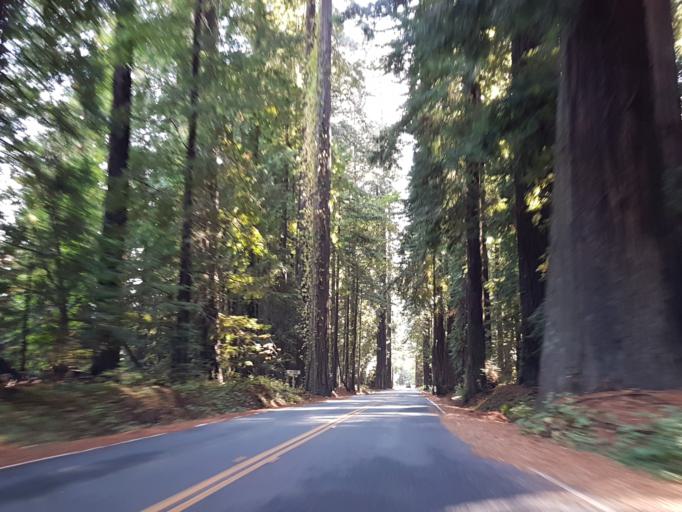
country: US
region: California
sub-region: Humboldt County
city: Rio Dell
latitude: 40.4360
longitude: -123.9851
